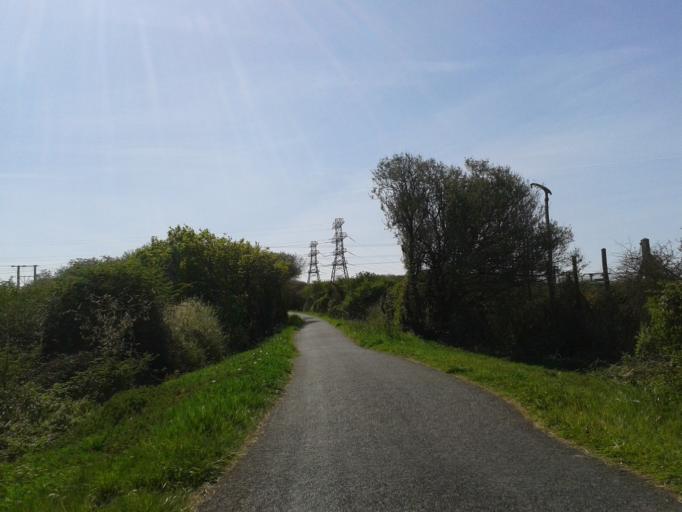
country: GB
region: England
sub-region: Devon
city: Appledore
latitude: 51.0690
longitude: -4.1688
